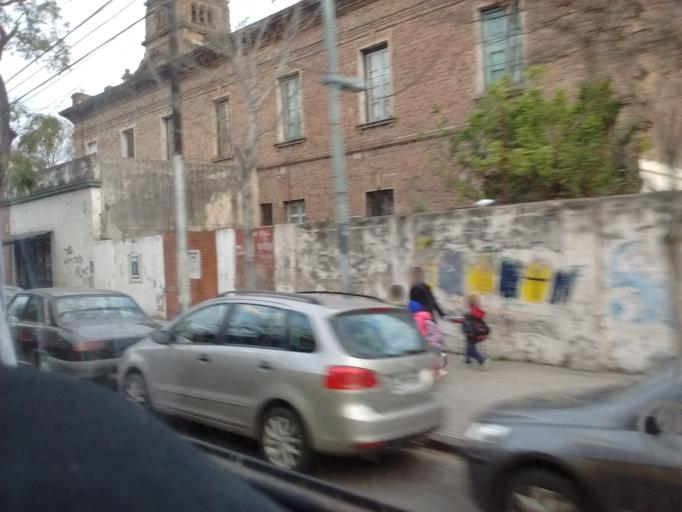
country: AR
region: Santa Fe
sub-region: Departamento de Rosario
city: Rosario
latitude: -32.9442
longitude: -60.6812
